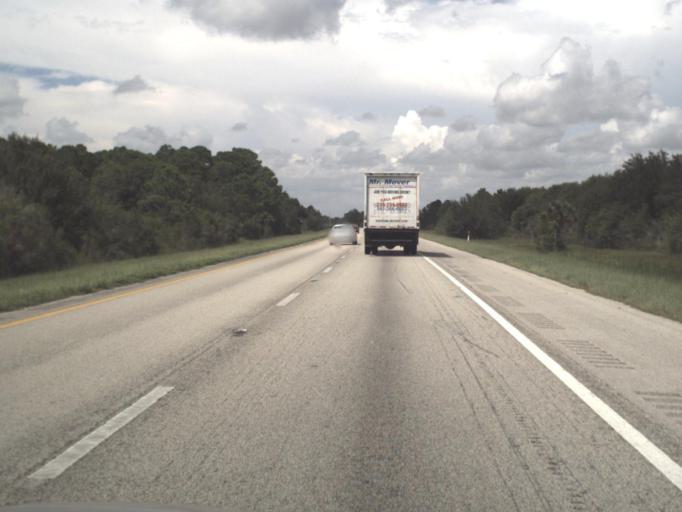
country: US
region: Florida
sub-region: Lee County
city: Suncoast Estates
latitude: 26.7906
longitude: -81.9039
